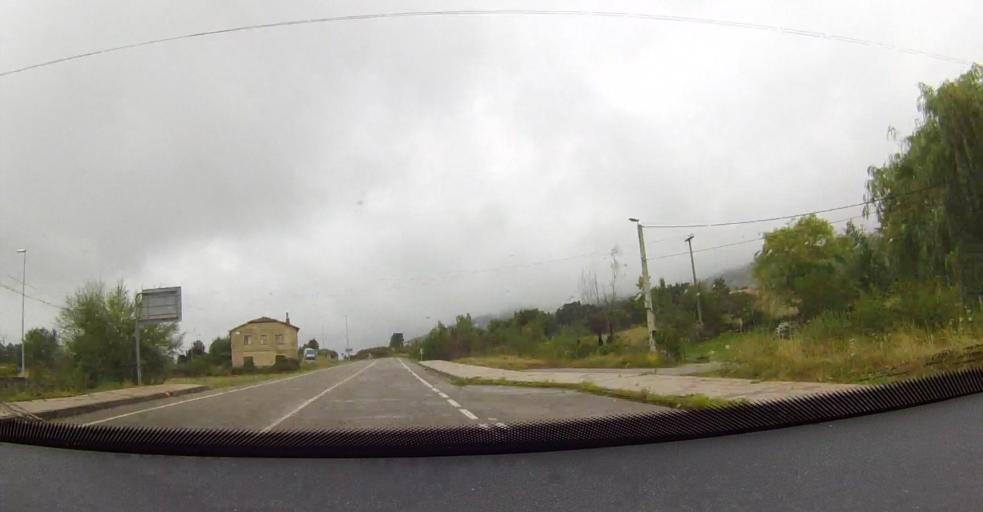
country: ES
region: Castille and Leon
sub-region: Provincia de Leon
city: Bonar
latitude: 42.8411
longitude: -5.2541
